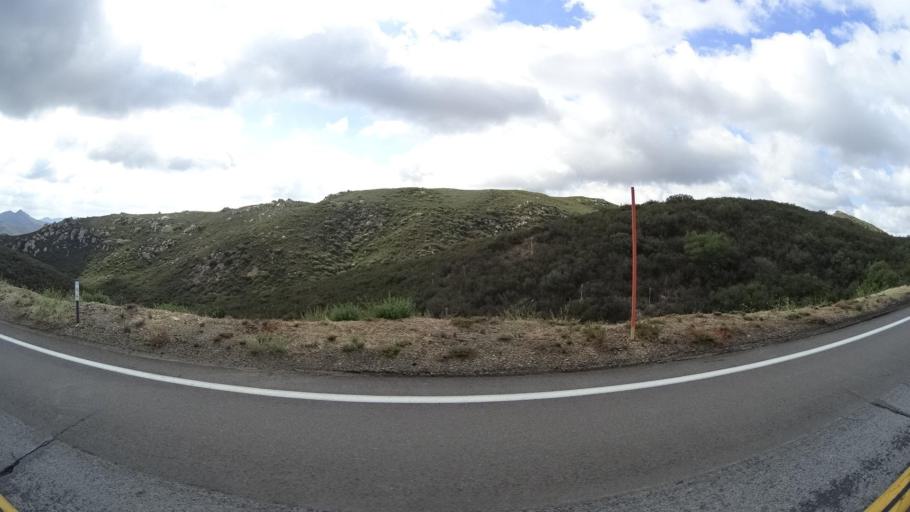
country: US
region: California
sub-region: San Diego County
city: Pine Valley
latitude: 32.8394
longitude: -116.4952
